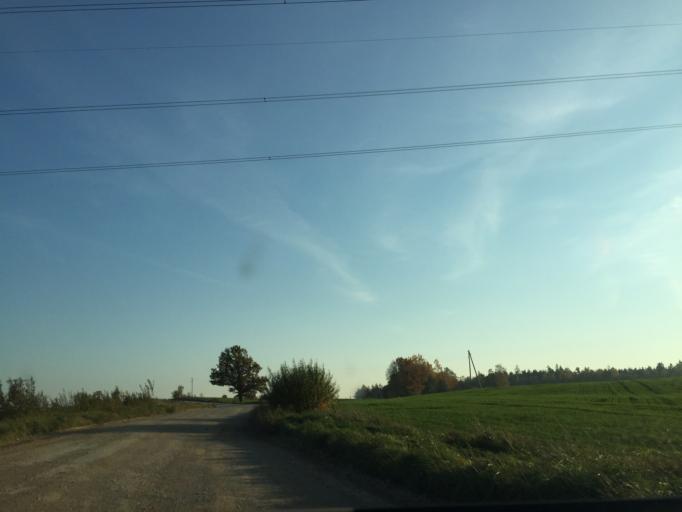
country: LV
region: Vainode
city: Vainode
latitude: 56.6148
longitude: 21.8162
